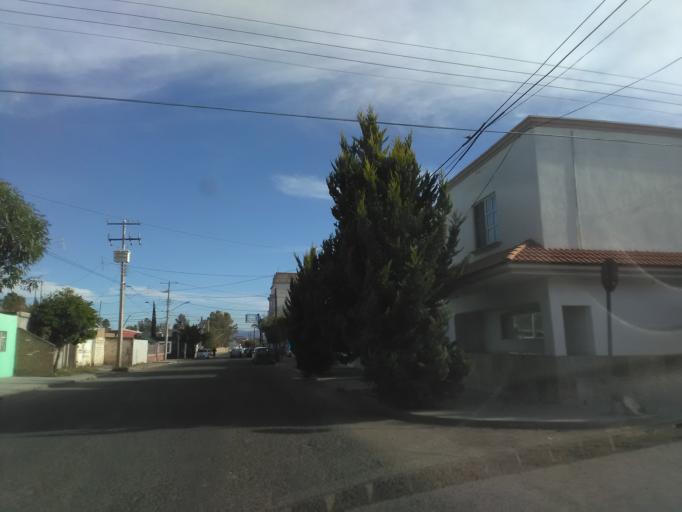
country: MX
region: Durango
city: Victoria de Durango
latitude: 24.0297
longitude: -104.6315
